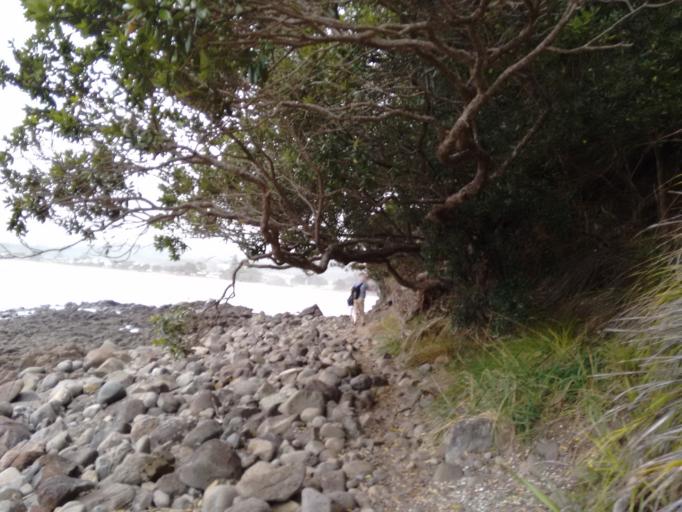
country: NZ
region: Waikato
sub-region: Thames-Coromandel District
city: Coromandel
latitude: -36.7036
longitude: 175.6104
